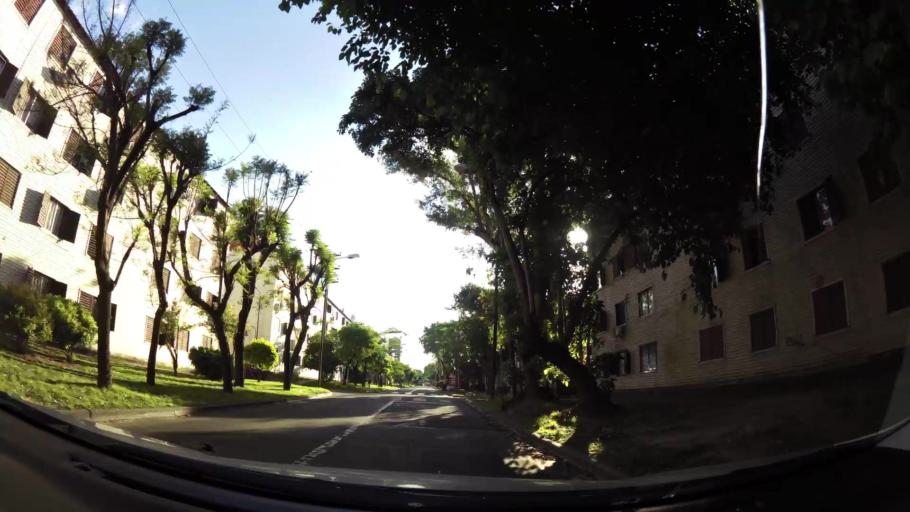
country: AR
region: Buenos Aires
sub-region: Partido de Tigre
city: Tigre
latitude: -34.4603
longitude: -58.5591
